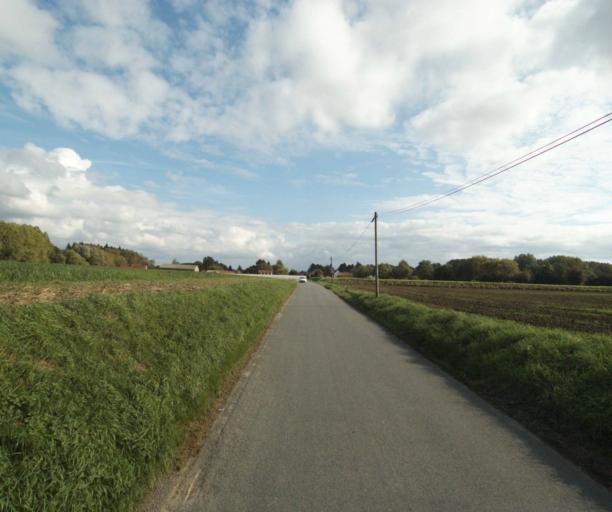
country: FR
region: Nord-Pas-de-Calais
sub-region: Departement du Nord
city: Ennetieres-en-Weppes
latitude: 50.6430
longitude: 2.9371
